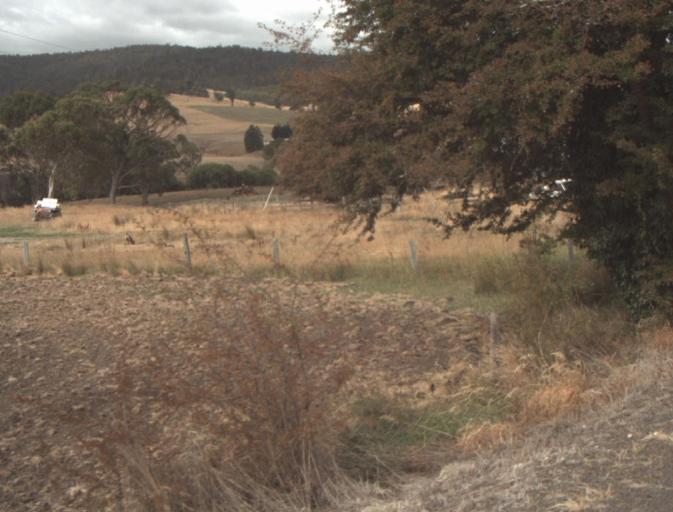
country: AU
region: Tasmania
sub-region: Dorset
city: Scottsdale
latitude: -41.4672
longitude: 147.5846
